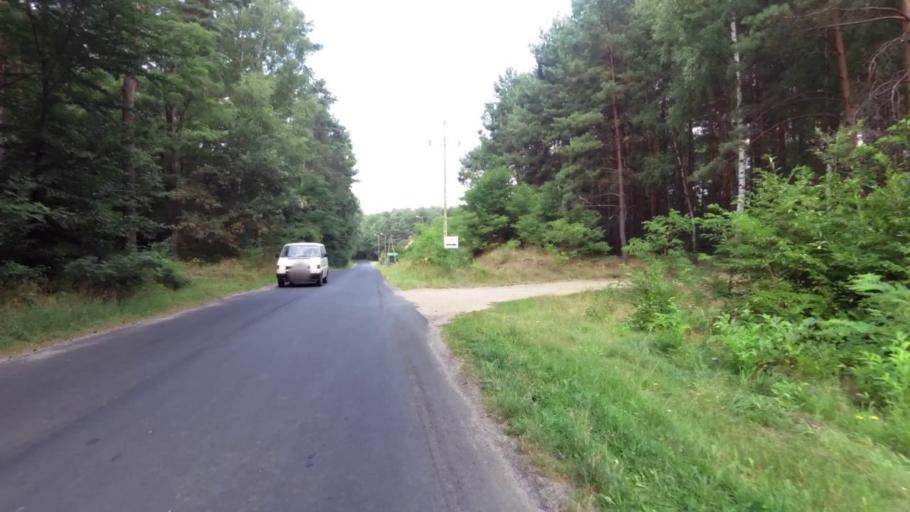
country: PL
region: West Pomeranian Voivodeship
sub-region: Powiat mysliborski
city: Debno
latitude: 52.8503
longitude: 14.7331
